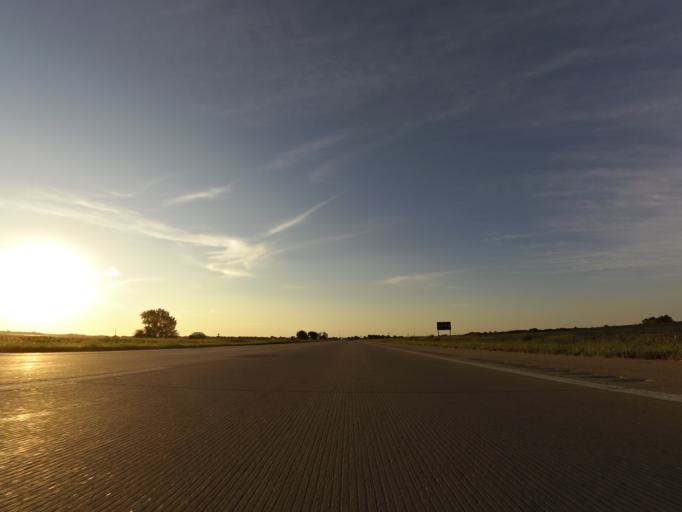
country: US
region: Kansas
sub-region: Reno County
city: Haven
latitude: 37.9075
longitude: -97.8039
